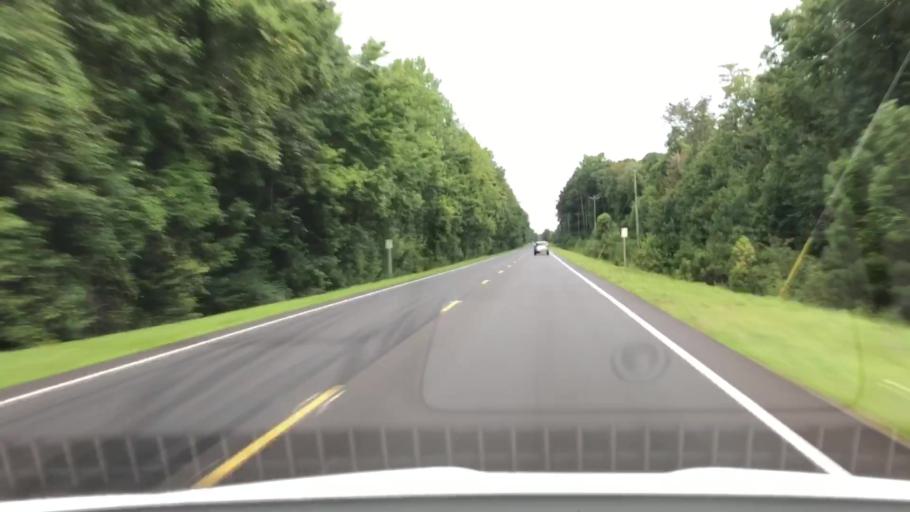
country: US
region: North Carolina
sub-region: Jones County
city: Maysville
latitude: 34.8724
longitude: -77.1972
